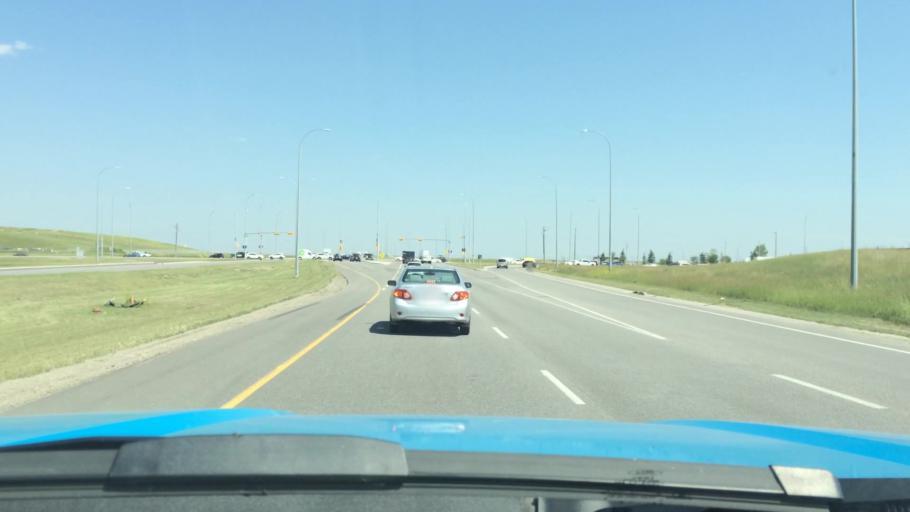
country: CA
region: Alberta
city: Calgary
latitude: 51.0147
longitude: -113.9616
